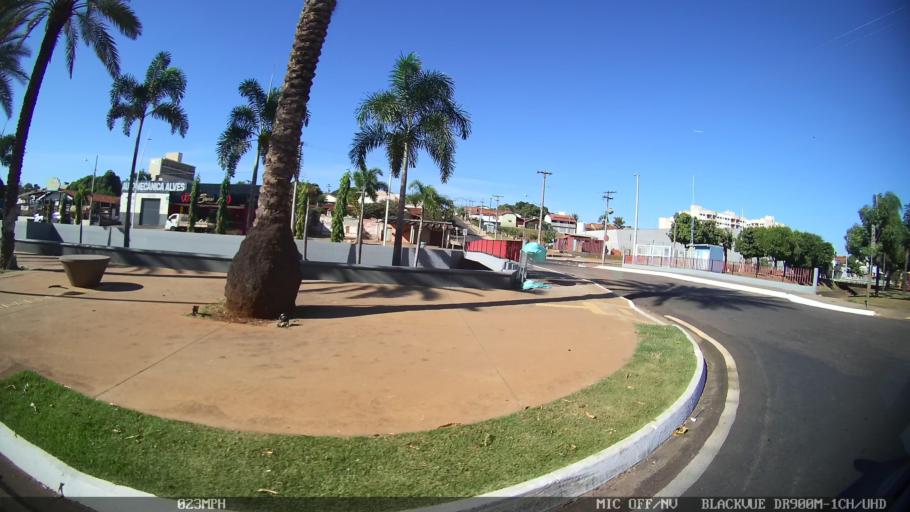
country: BR
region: Sao Paulo
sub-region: Olimpia
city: Olimpia
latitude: -20.7348
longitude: -48.9121
